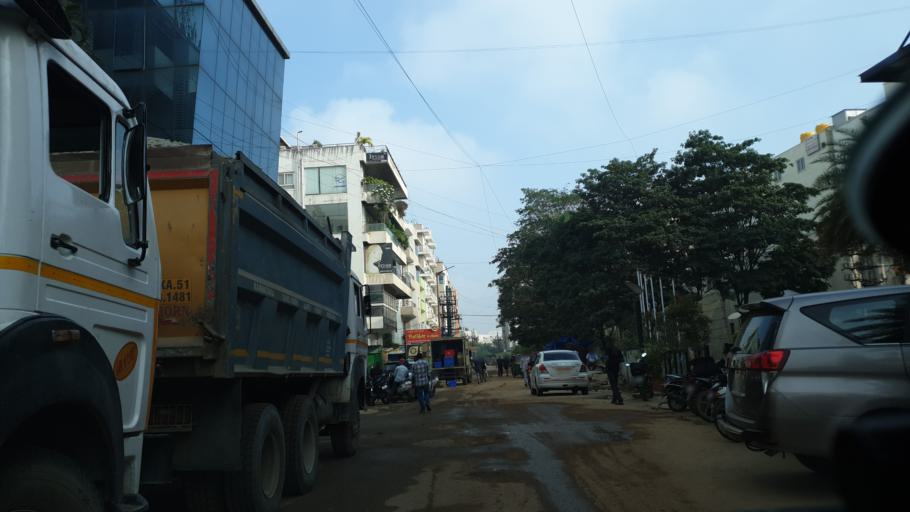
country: IN
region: Karnataka
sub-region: Bangalore Urban
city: Bangalore
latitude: 12.9573
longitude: 77.7091
